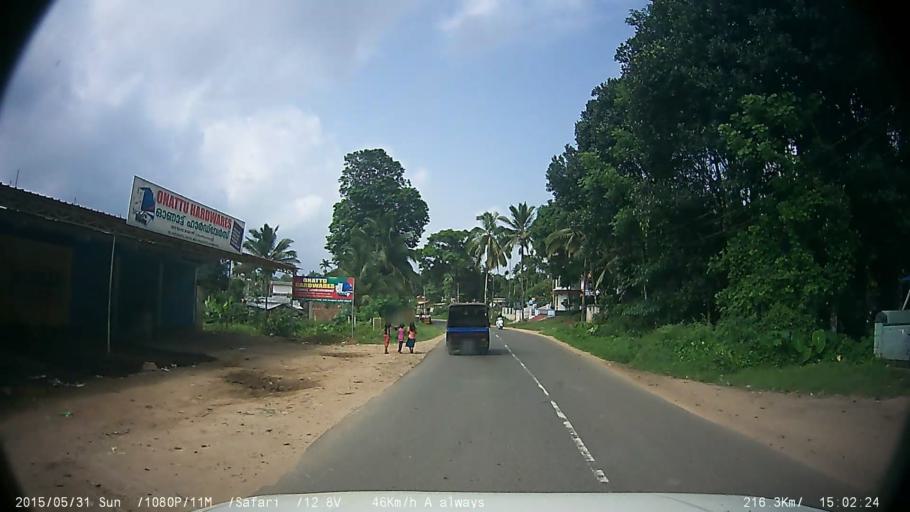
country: IN
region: Kerala
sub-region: Wayanad
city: Kalpetta
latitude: 11.6278
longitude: 76.2108
